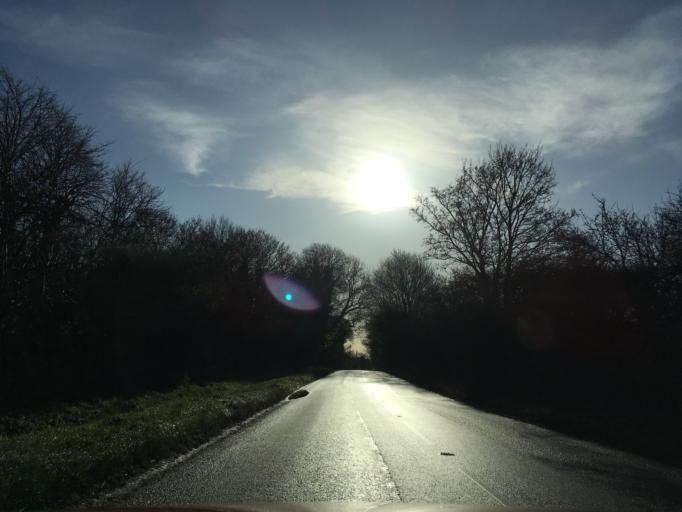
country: GB
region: England
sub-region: Wiltshire
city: Collingbourne Kingston
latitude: 51.2924
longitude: -1.6544
